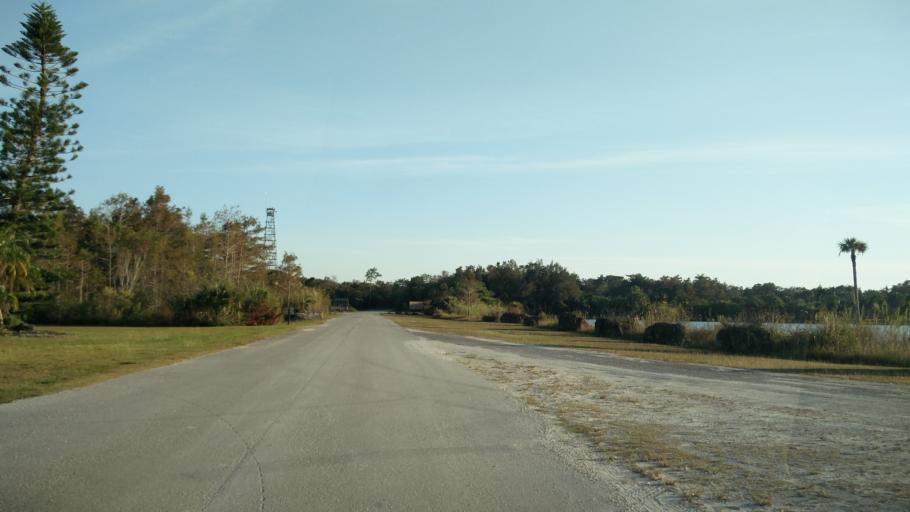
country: US
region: Florida
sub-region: Collier County
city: Lely Resort
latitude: 25.9529
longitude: -81.3613
